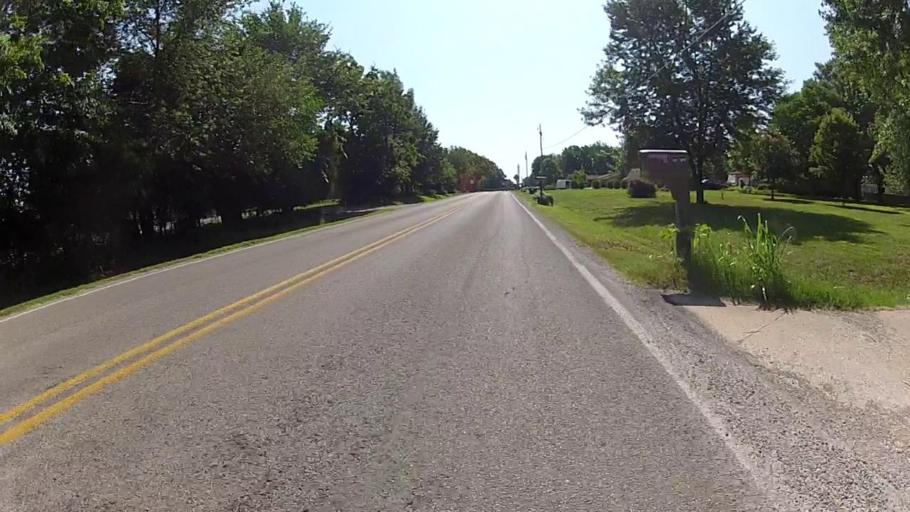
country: US
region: Kansas
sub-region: Montgomery County
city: Independence
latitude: 37.1928
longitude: -95.7136
